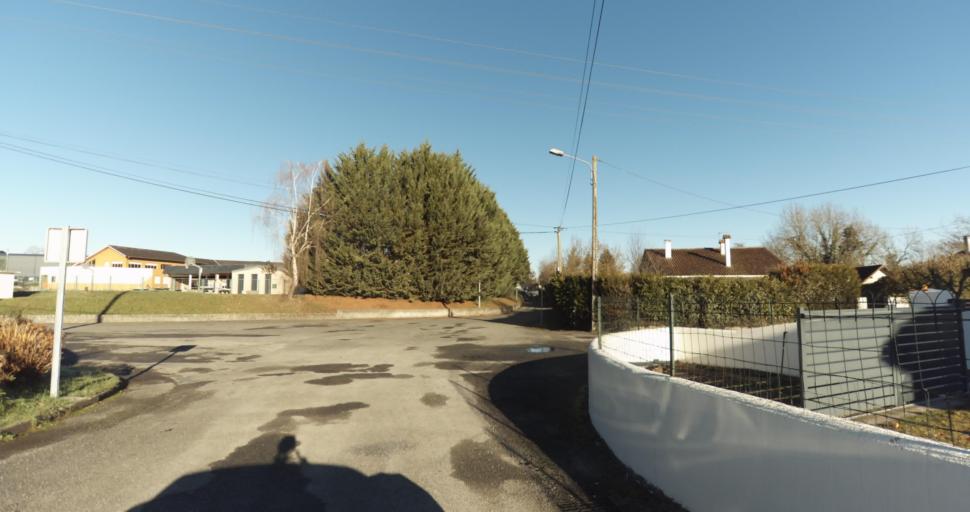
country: FR
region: Aquitaine
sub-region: Departement des Pyrenees-Atlantiques
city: Morlaas
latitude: 43.3408
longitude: -0.2601
